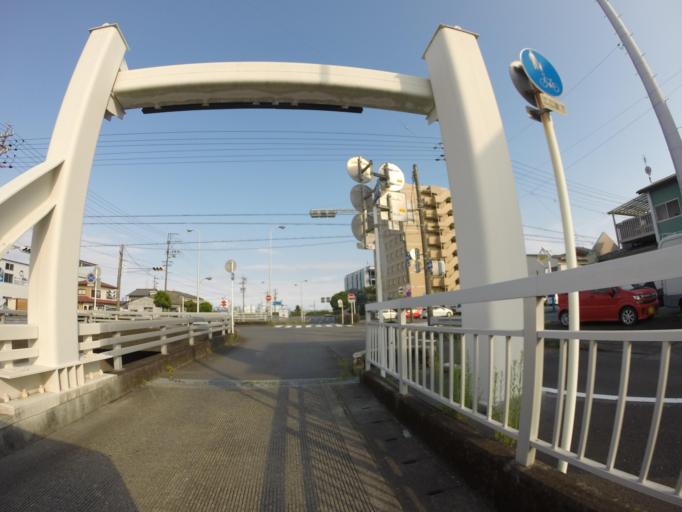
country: JP
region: Shizuoka
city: Shizuoka-shi
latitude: 35.0344
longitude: 138.4945
